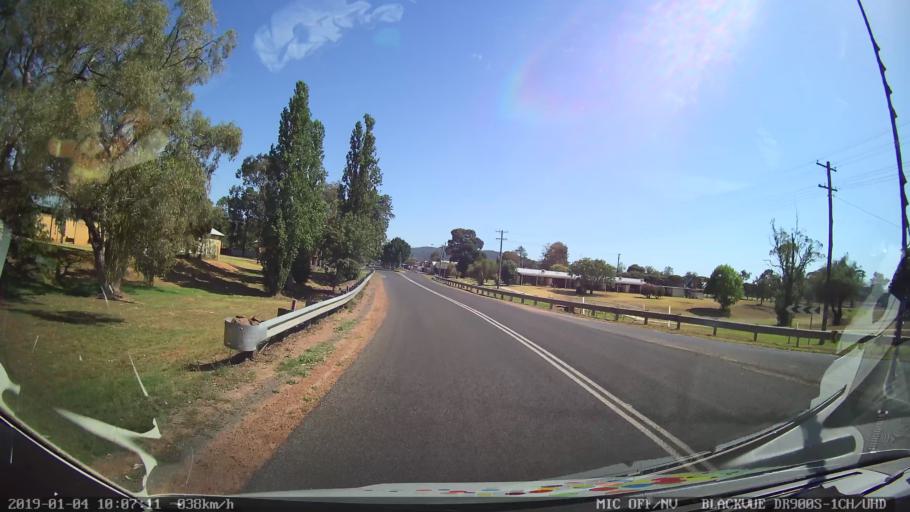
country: AU
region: New South Wales
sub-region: Cabonne
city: Canowindra
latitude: -33.4297
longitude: 148.3715
